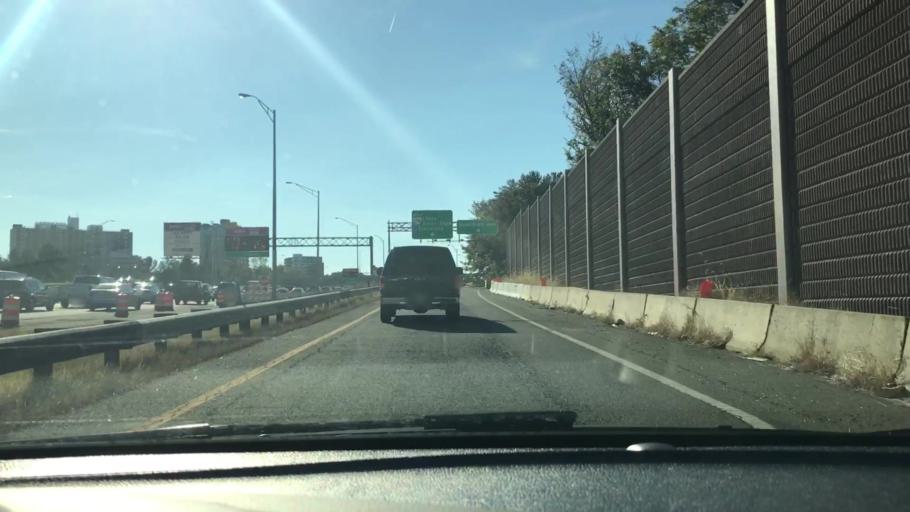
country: US
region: Virginia
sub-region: Fairfax County
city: Lincolnia
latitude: 38.8181
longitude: -77.1331
